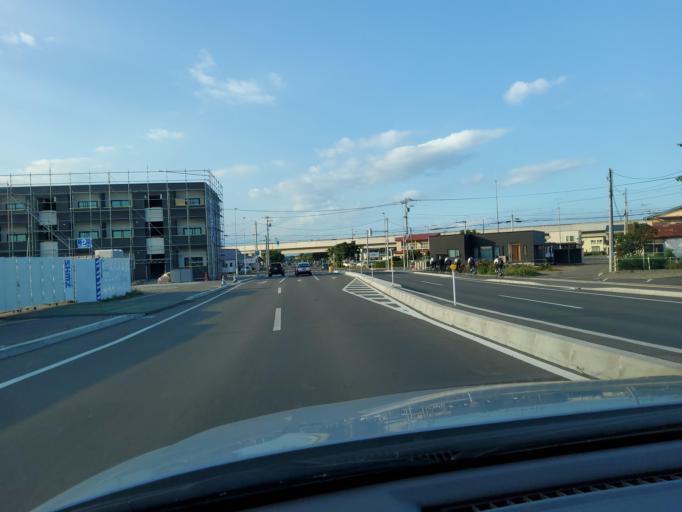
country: JP
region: Hokkaido
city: Obihiro
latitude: 42.9241
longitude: 143.1859
